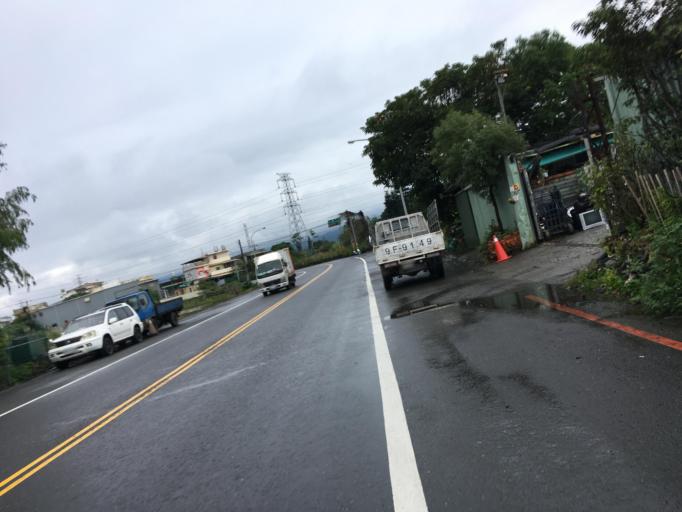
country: TW
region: Taiwan
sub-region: Yilan
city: Yilan
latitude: 24.6652
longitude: 121.7497
